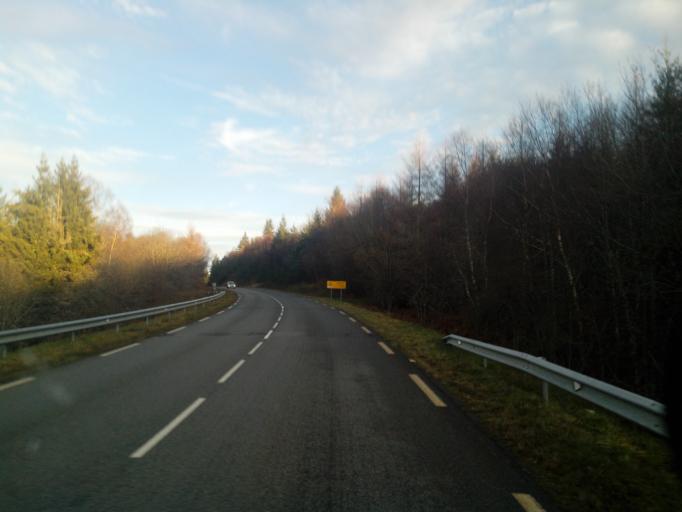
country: FR
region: Limousin
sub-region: Departement de la Correze
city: Meymac
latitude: 45.5769
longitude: 2.1000
